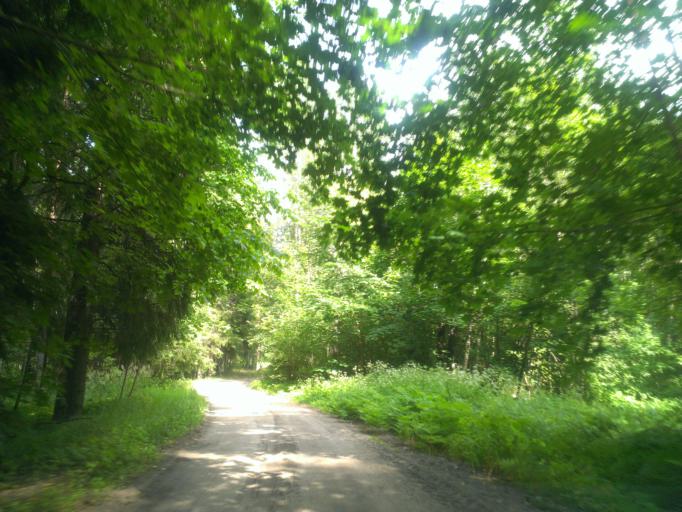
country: LV
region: Ligatne
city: Ligatne
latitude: 57.2346
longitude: 25.0298
